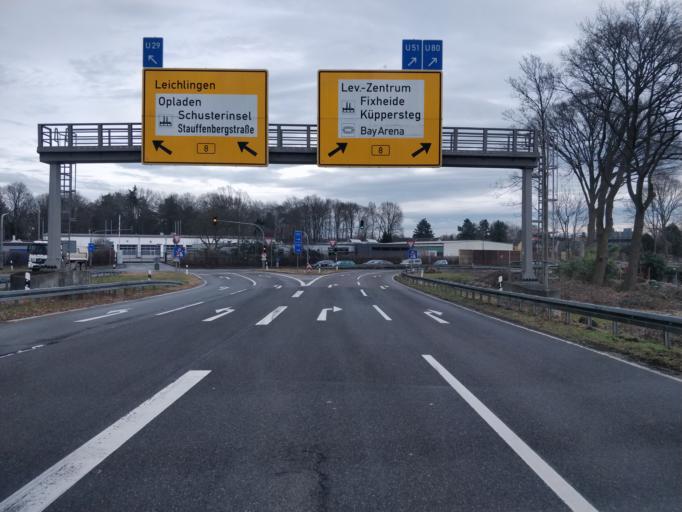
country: DE
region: North Rhine-Westphalia
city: Opladen
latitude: 51.0563
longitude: 6.9931
